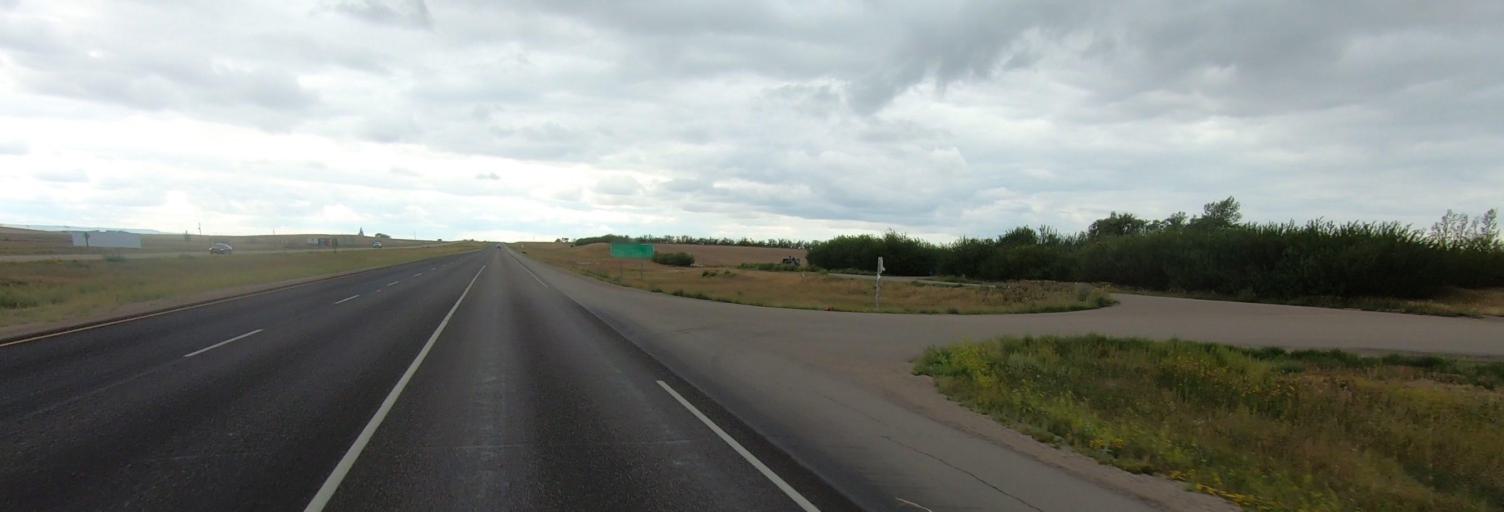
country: CA
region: Saskatchewan
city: Shaunavon
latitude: 50.1010
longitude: -108.4888
